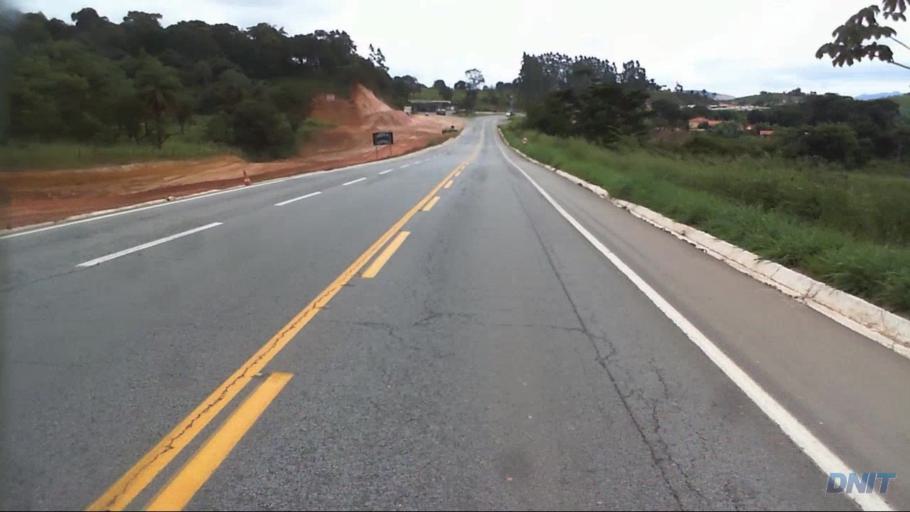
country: BR
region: Minas Gerais
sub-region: Caete
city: Caete
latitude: -19.7429
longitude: -43.5522
